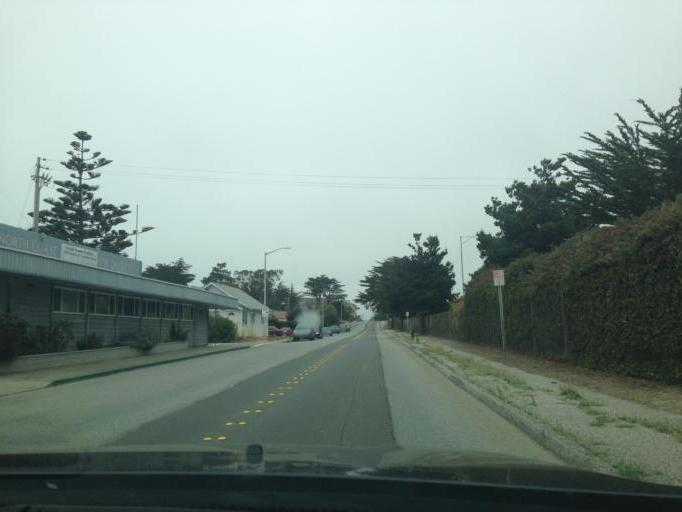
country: US
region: California
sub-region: San Mateo County
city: Pacifica
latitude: 37.6302
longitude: -122.4898
